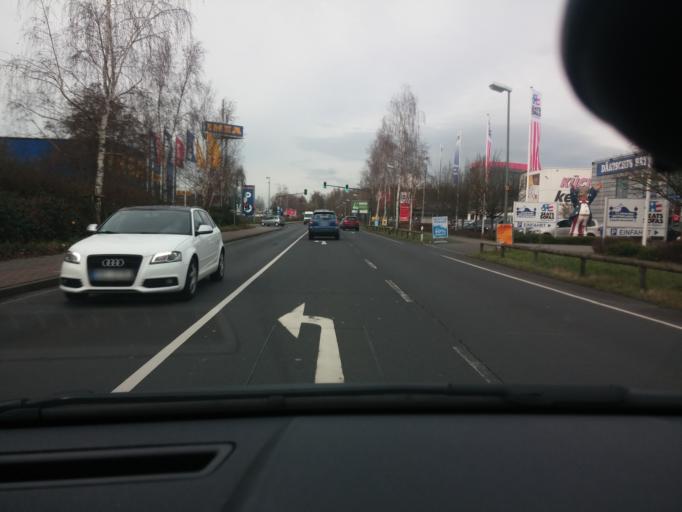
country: DE
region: Hesse
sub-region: Regierungsbezirk Darmstadt
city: Erlensee
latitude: 50.1486
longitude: 8.9474
